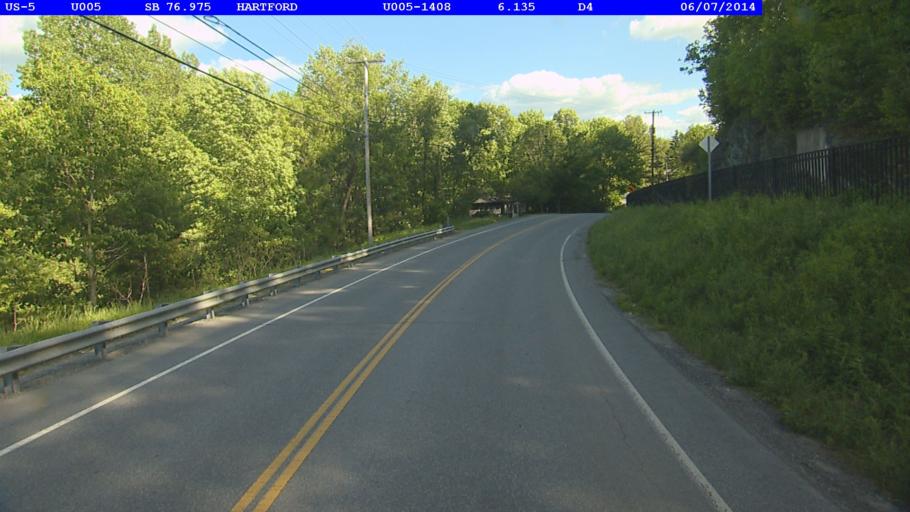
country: US
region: Vermont
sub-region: Windsor County
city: Wilder
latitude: 43.6796
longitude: -72.3109
